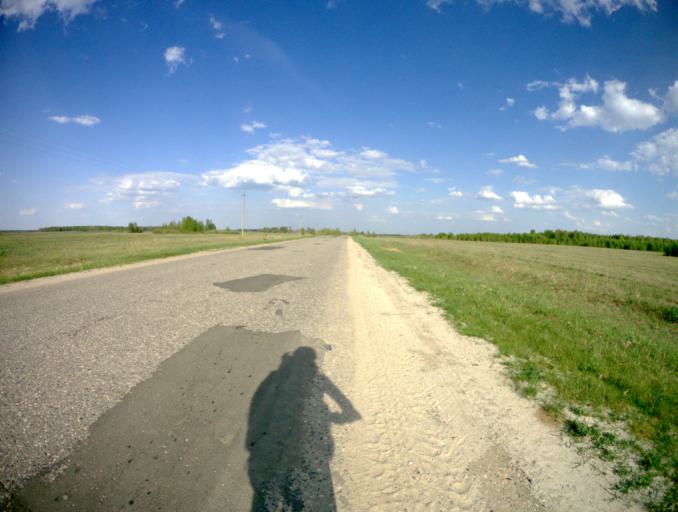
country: RU
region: Ivanovo
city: Kolobovo
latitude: 56.5402
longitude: 41.5197
